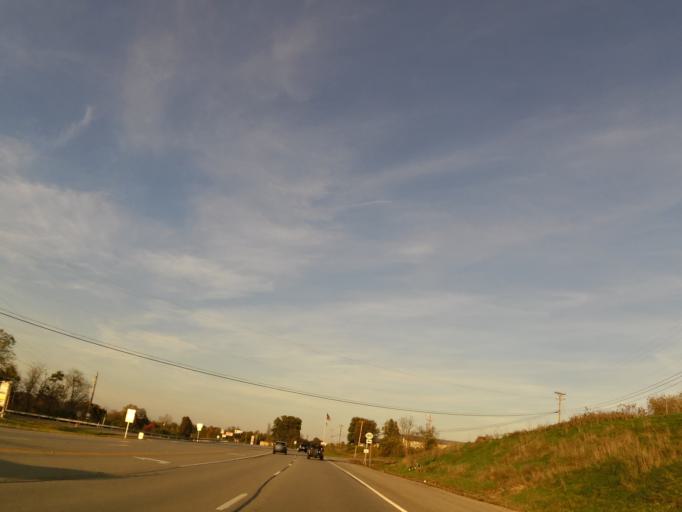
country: US
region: Kentucky
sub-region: Jessamine County
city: Wilmore
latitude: 37.7498
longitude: -84.6207
